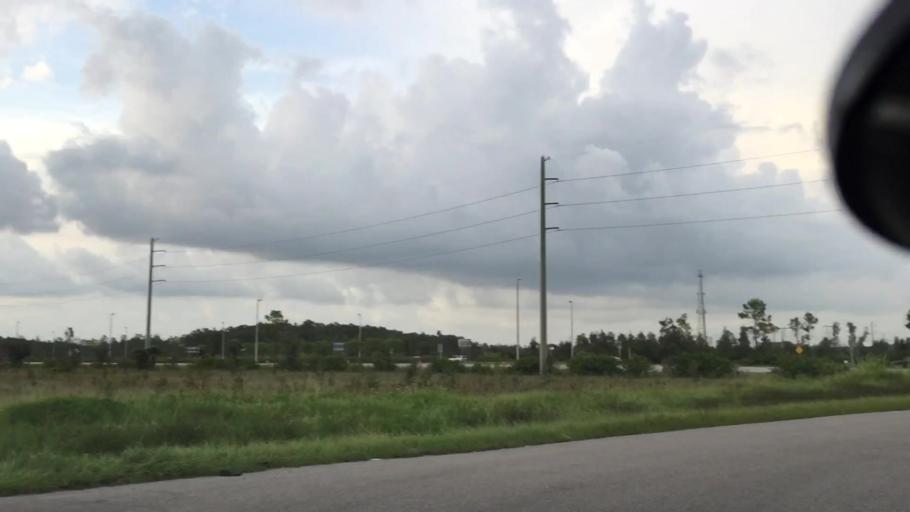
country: US
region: Florida
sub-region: Lee County
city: Gateway
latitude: 26.6192
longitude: -81.7702
